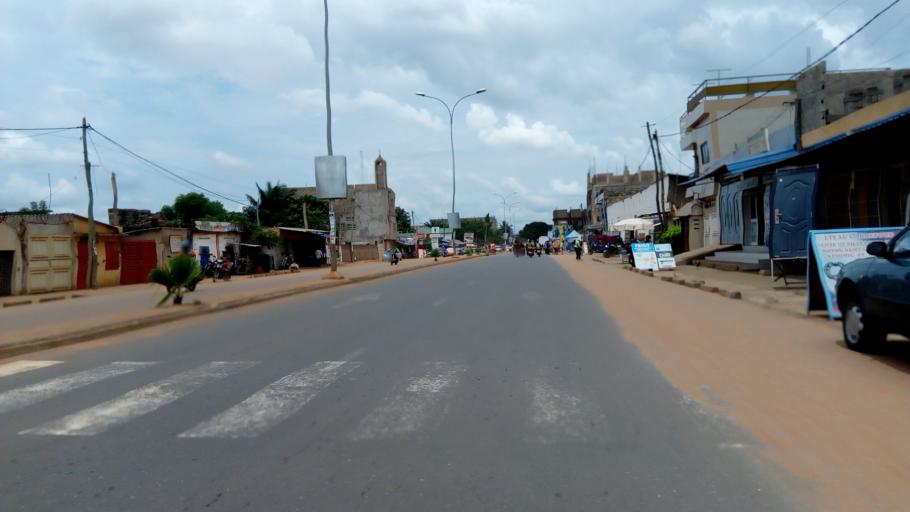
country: TG
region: Maritime
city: Lome
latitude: 6.2175
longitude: 1.1703
